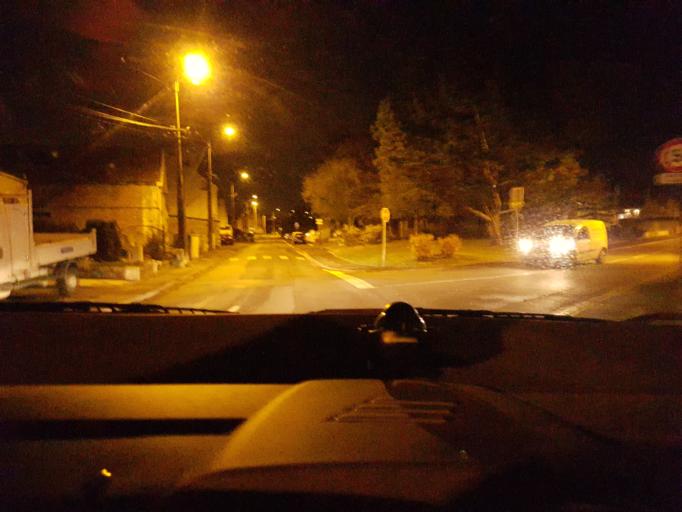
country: FR
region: Nord-Pas-de-Calais
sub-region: Departement du Pas-de-Calais
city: Bully-les-Mines
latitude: 50.4392
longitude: 2.7208
